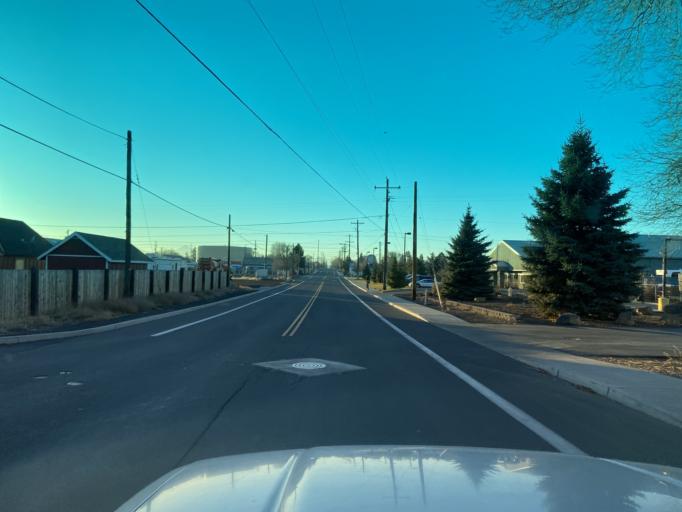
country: US
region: Oregon
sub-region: Deschutes County
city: Redmond
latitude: 44.2766
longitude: -121.1643
